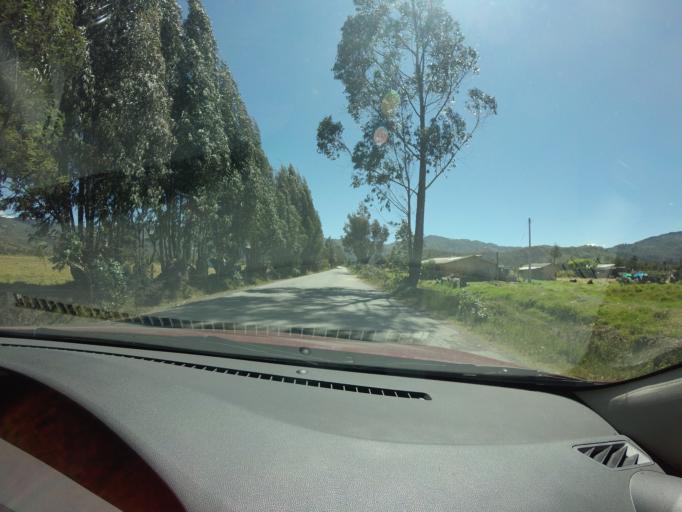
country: CO
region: Cundinamarca
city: Cucunuba
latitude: 5.2601
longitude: -73.7869
